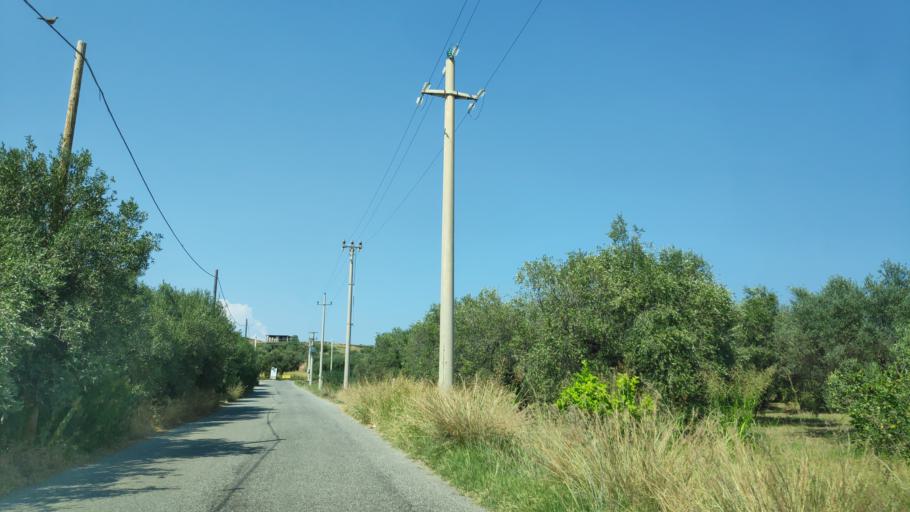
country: IT
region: Calabria
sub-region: Provincia di Reggio Calabria
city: Monasterace Marina
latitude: 38.4260
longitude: 16.5437
